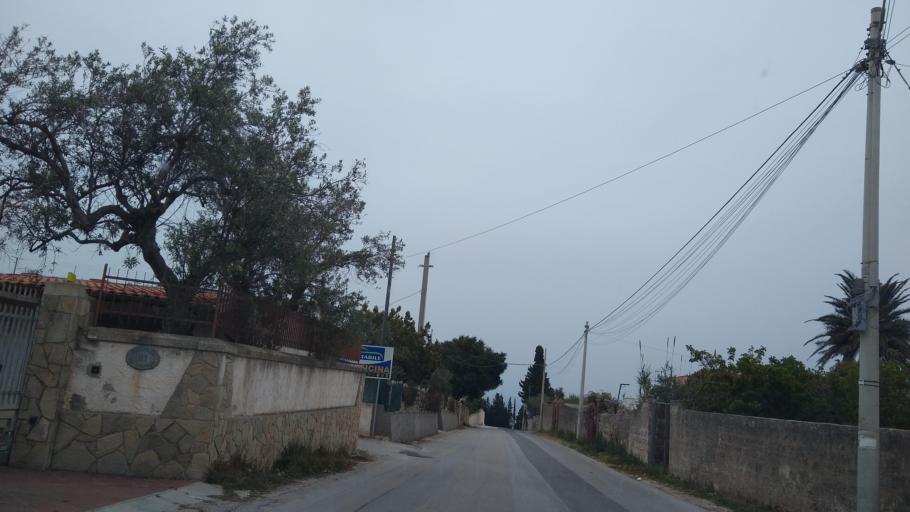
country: IT
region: Sicily
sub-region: Trapani
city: Castellammare del Golfo
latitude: 38.0183
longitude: 12.8973
